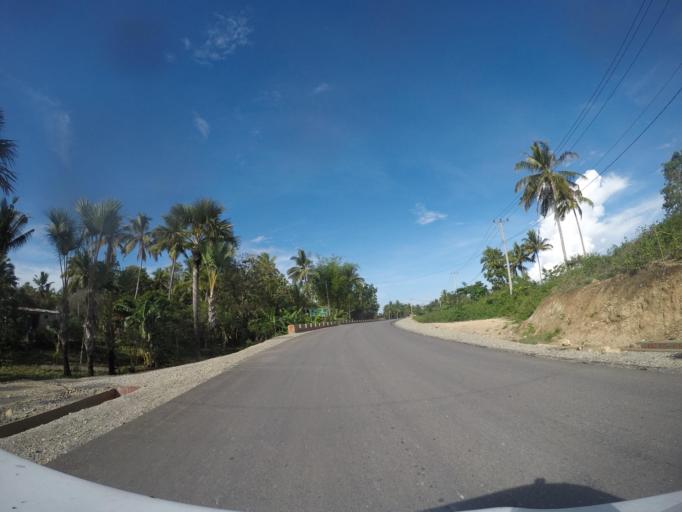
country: TL
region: Baucau
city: Baucau
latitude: -8.5049
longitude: 126.4453
